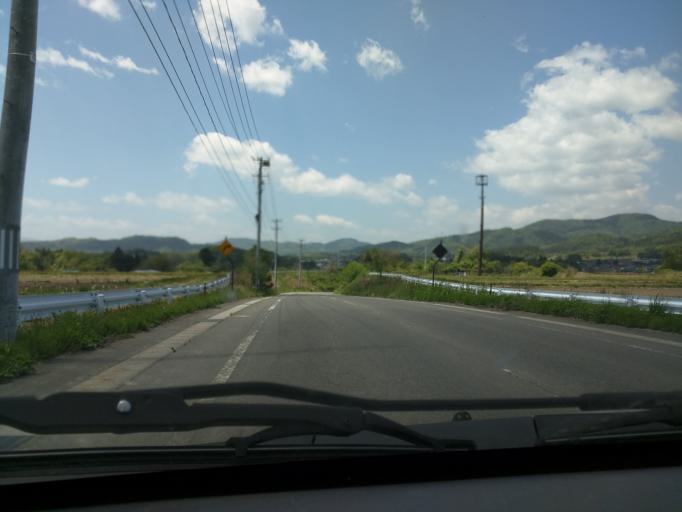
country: JP
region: Fukushima
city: Kitakata
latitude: 37.6387
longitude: 139.7817
